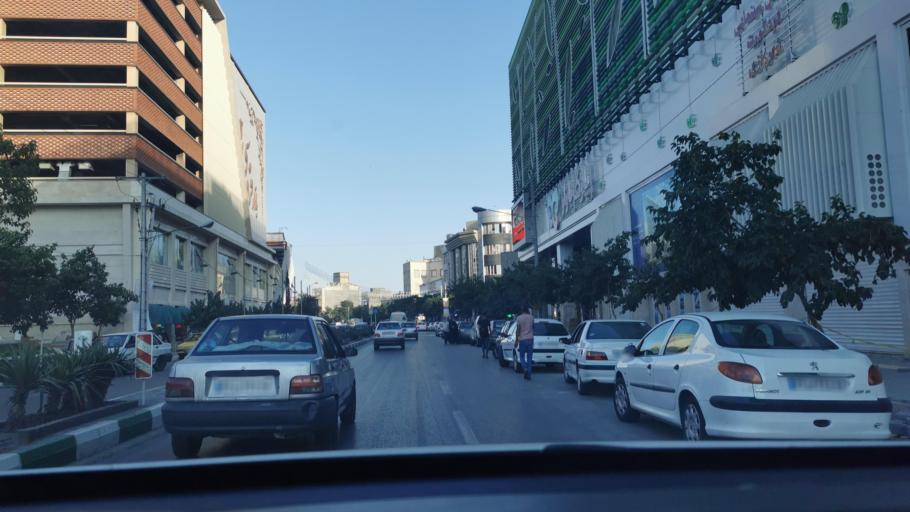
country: IR
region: Razavi Khorasan
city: Mashhad
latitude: 36.2922
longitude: 59.6470
